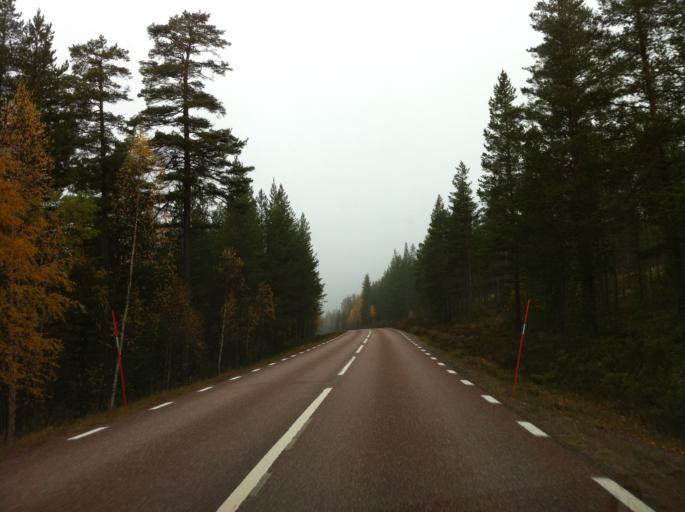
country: NO
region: Hedmark
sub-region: Trysil
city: Innbygda
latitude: 61.7817
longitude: 12.9391
